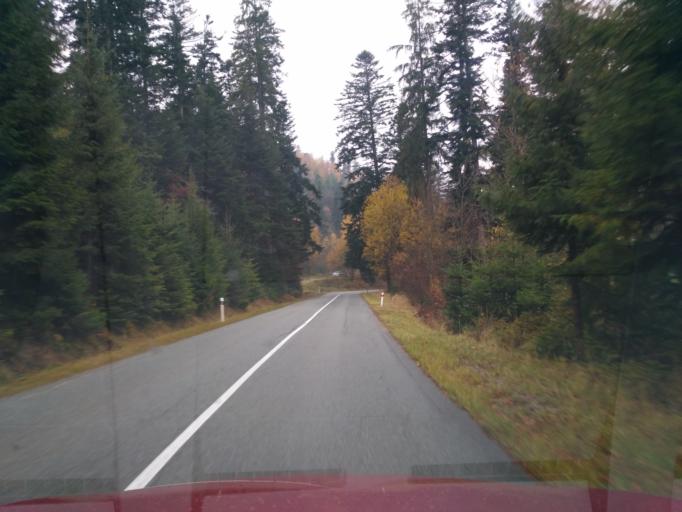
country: SK
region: Kosicky
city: Medzev
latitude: 48.7224
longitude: 20.7384
